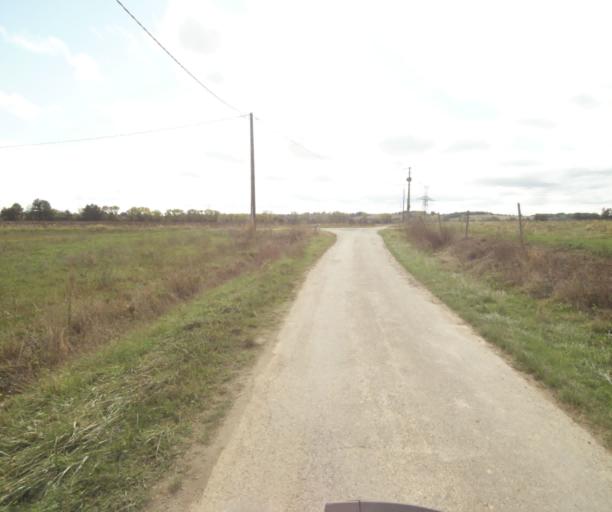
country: FR
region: Midi-Pyrenees
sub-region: Departement du Tarn-et-Garonne
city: Verdun-sur-Garonne
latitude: 43.8634
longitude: 1.1963
